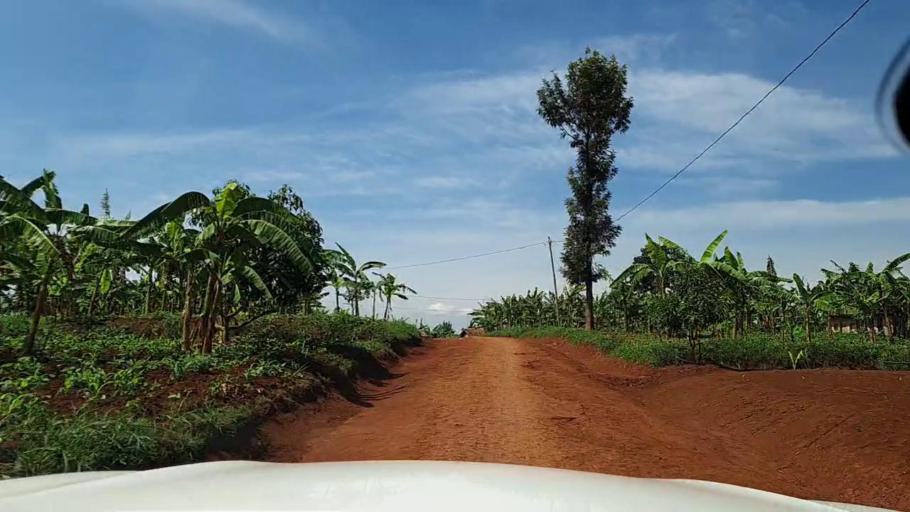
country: RW
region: Southern Province
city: Butare
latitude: -2.7021
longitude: 29.8488
